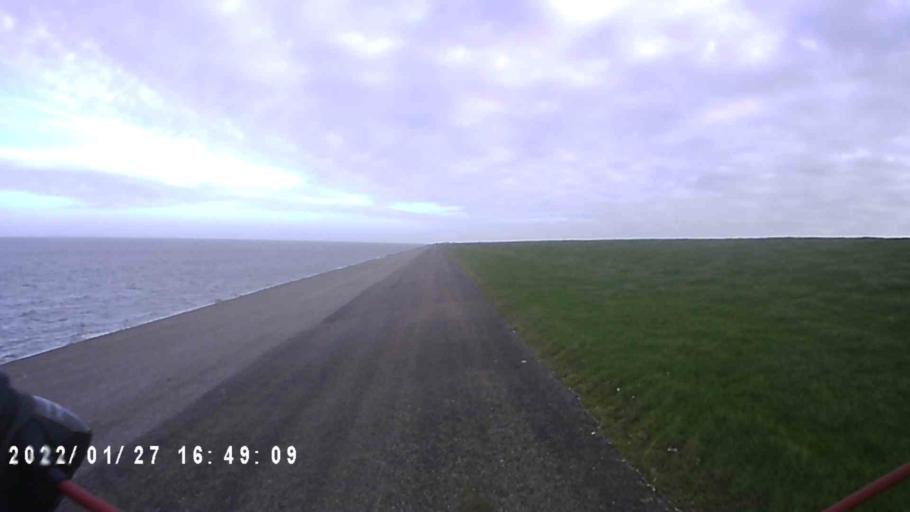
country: NL
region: Friesland
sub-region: Gemeente Dongeradeel
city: Ternaard
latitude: 53.4037
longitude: 6.0413
